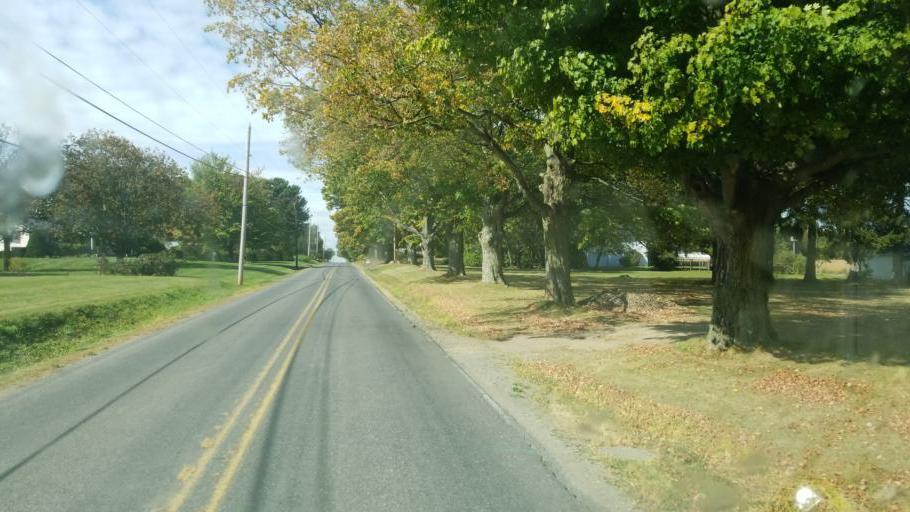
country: US
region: Pennsylvania
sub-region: Mercer County
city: Greenville
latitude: 41.4022
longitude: -80.4106
